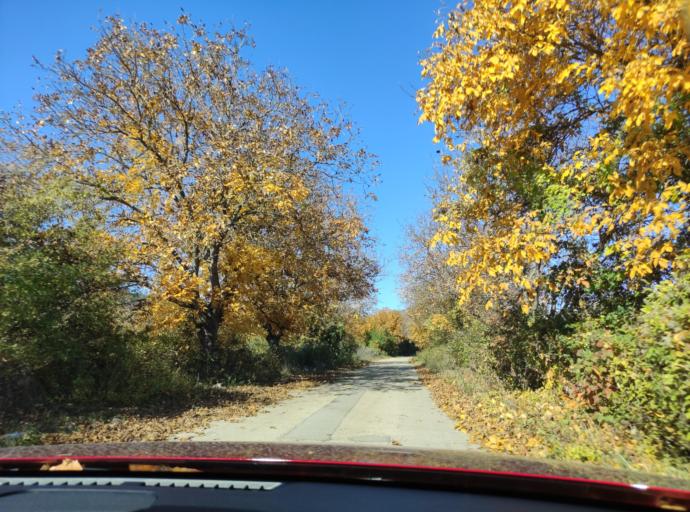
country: BG
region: Montana
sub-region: Obshtina Montana
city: Montana
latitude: 43.4301
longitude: 23.0619
